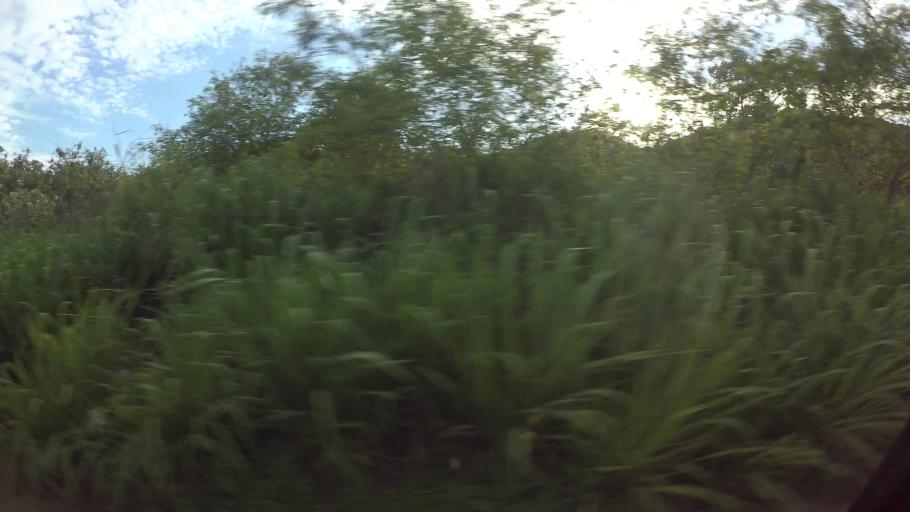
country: TH
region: Chon Buri
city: Sattahip
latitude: 12.6826
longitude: 100.9271
